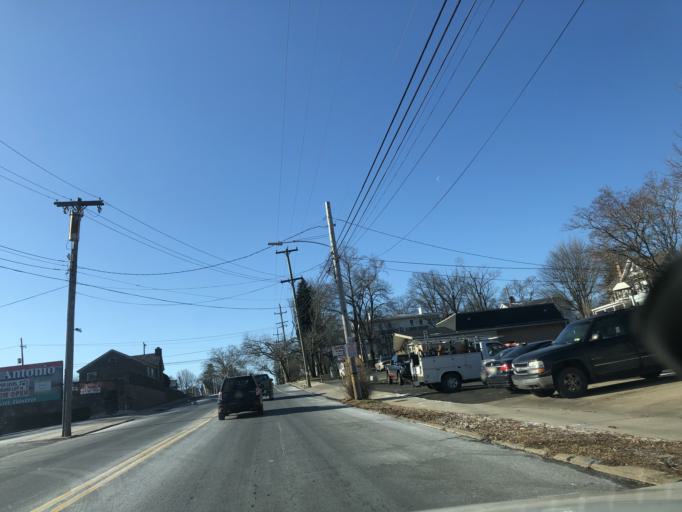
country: US
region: Pennsylvania
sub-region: Bucks County
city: Morrisville
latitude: 40.2179
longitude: -74.7806
